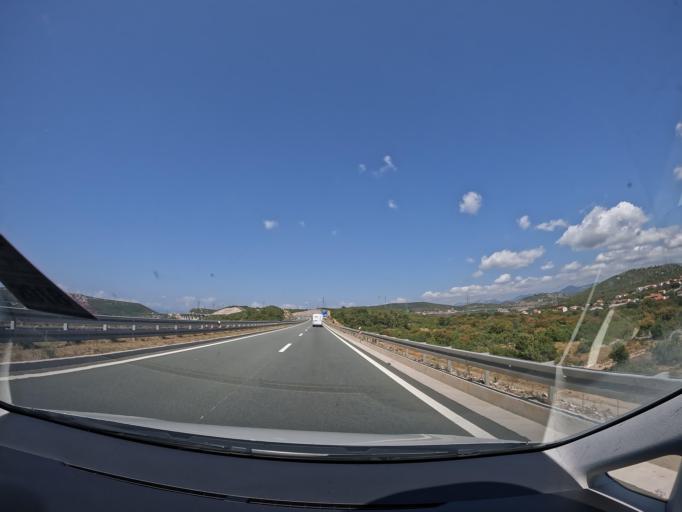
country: HR
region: Primorsko-Goranska
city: Krasica
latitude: 45.3090
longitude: 14.5521
